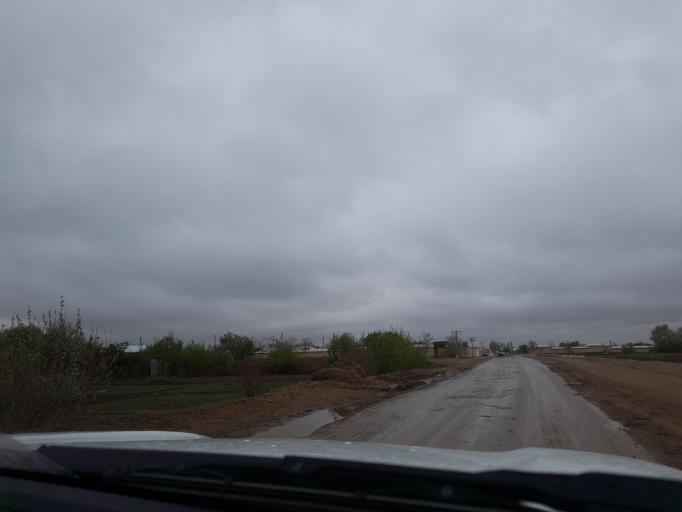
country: TM
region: Lebap
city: Sayat
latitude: 38.4530
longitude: 64.3634
